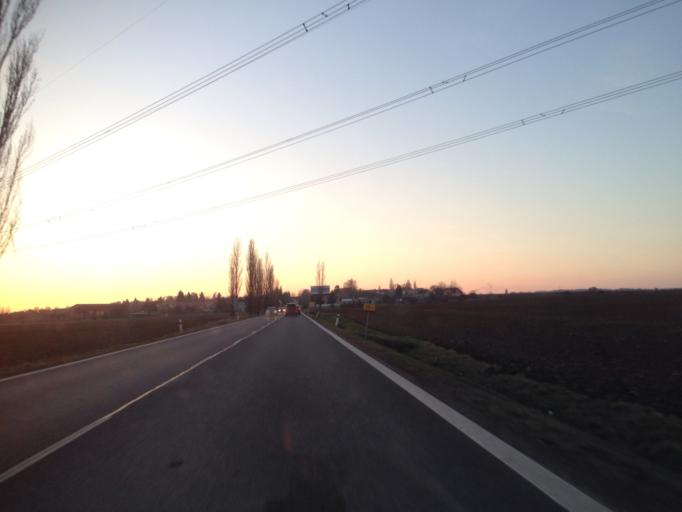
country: CZ
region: Central Bohemia
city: Revnicov
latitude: 50.1781
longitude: 13.8178
